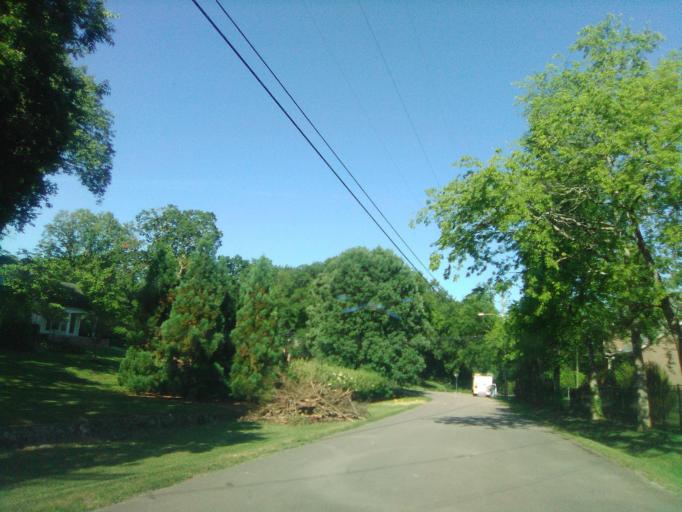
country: US
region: Tennessee
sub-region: Davidson County
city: Belle Meade
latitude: 36.1204
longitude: -86.8367
